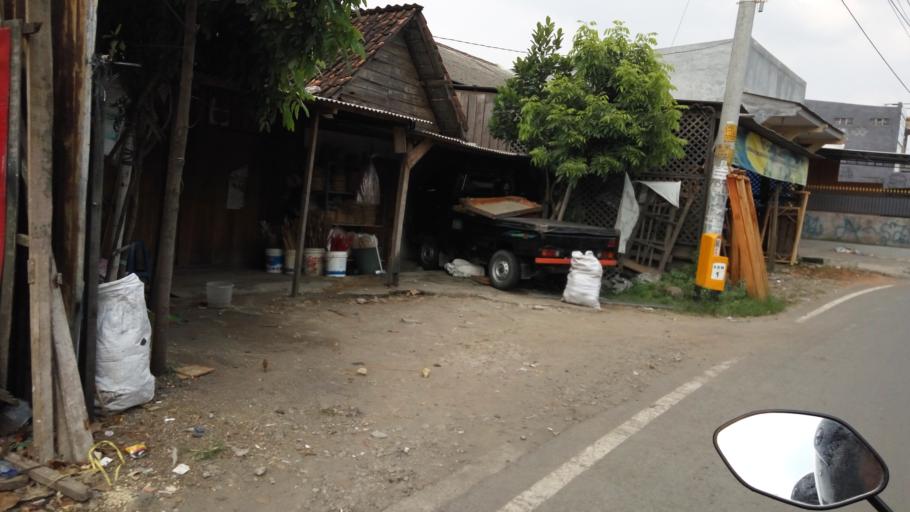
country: ID
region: Central Java
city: Mranggen
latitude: -7.0361
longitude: 110.4678
